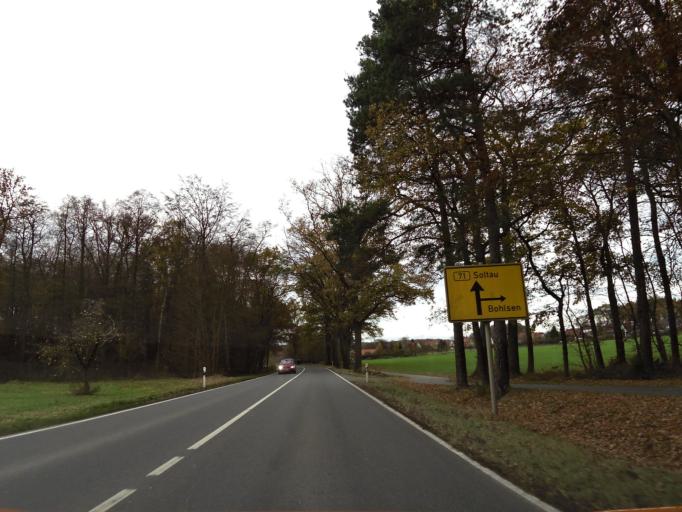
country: DE
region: Lower Saxony
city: Schwienau
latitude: 52.9597
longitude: 10.4682
